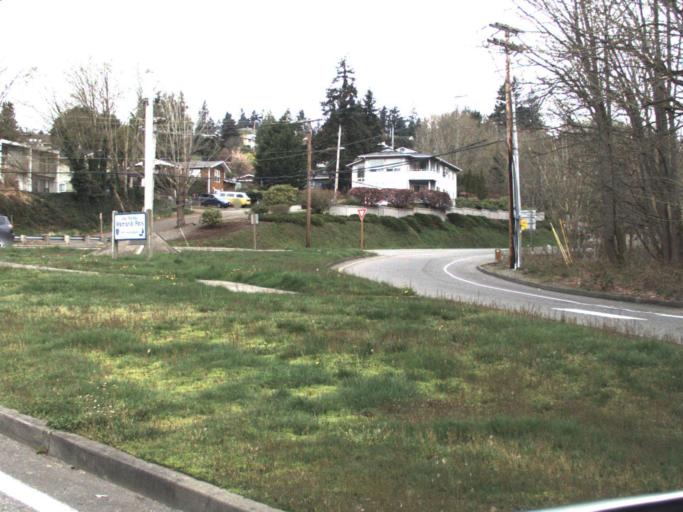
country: US
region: Washington
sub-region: King County
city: Des Moines
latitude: 47.4085
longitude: -122.3265
